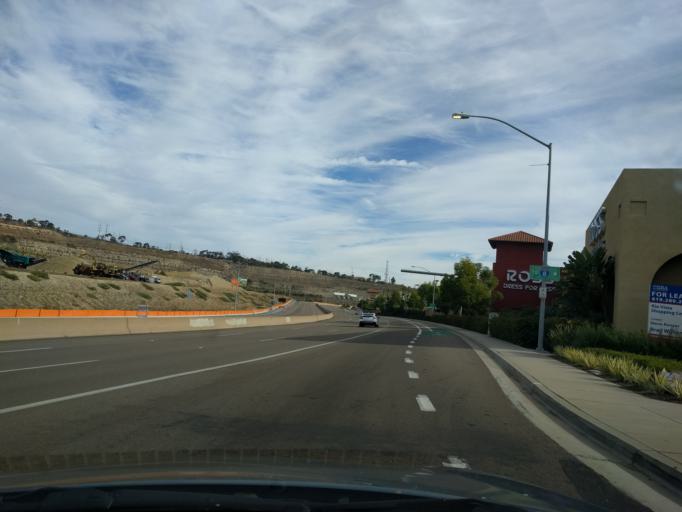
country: US
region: California
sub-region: San Diego County
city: San Diego
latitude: 32.7754
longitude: -117.1469
